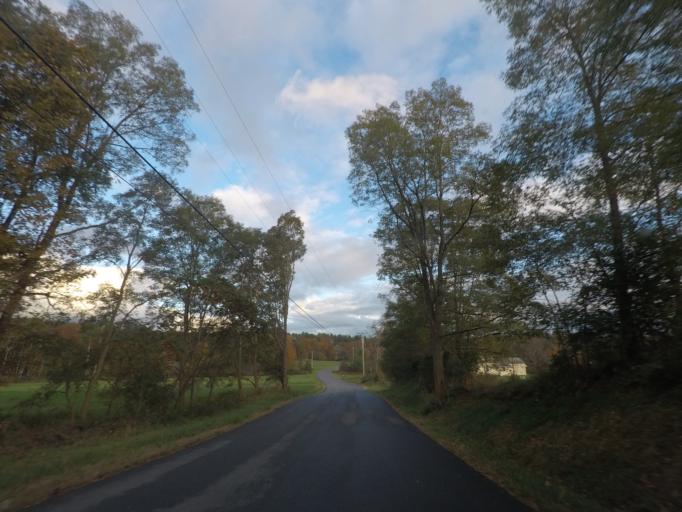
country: US
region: New York
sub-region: Rensselaer County
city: Nassau
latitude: 42.5558
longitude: -73.5991
